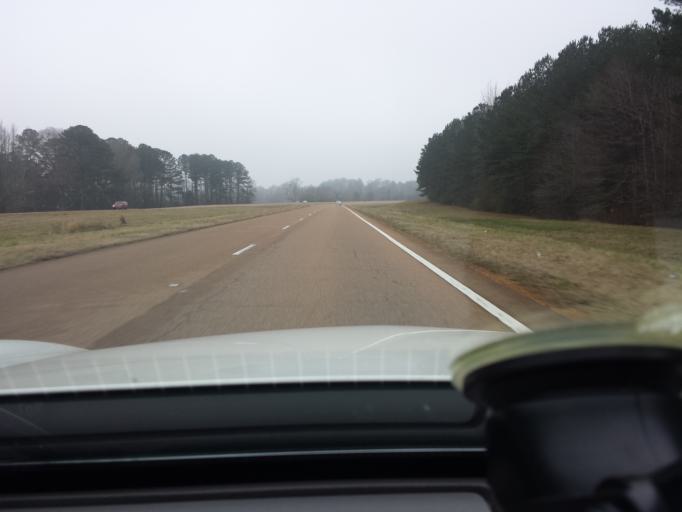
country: US
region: Mississippi
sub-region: Winston County
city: Louisville
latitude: 33.1813
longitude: -89.0123
